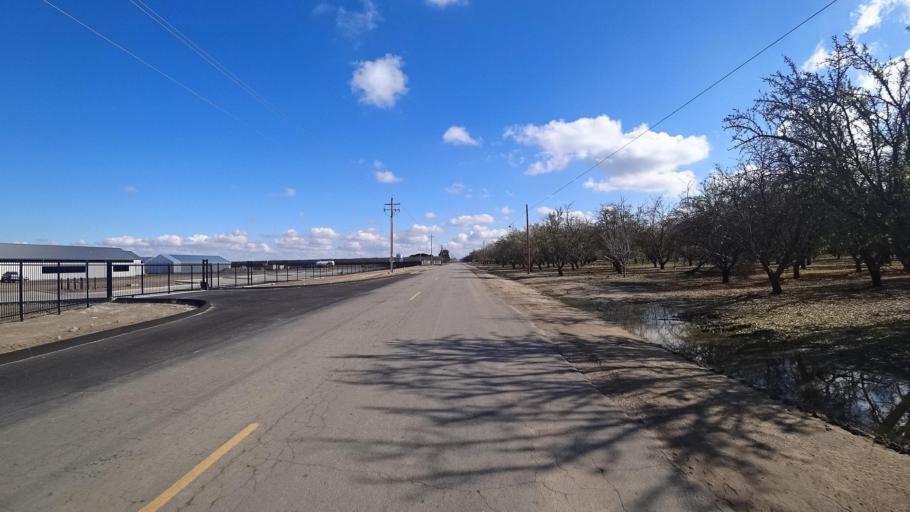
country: US
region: California
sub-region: Kern County
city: McFarland
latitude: 35.6887
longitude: -119.3058
